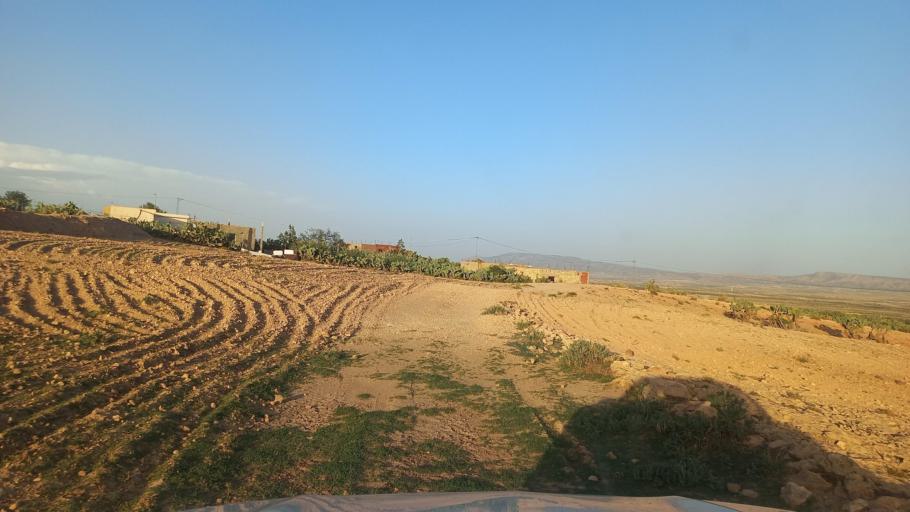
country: TN
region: Al Qasrayn
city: Sbiba
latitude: 35.3734
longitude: 9.0033
